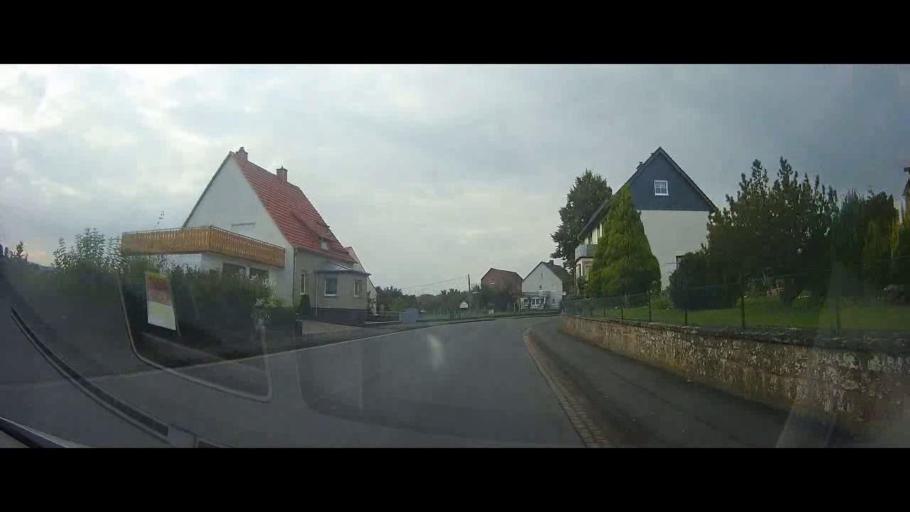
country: DE
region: Lower Saxony
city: Uslar
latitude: 51.6071
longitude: 9.6740
